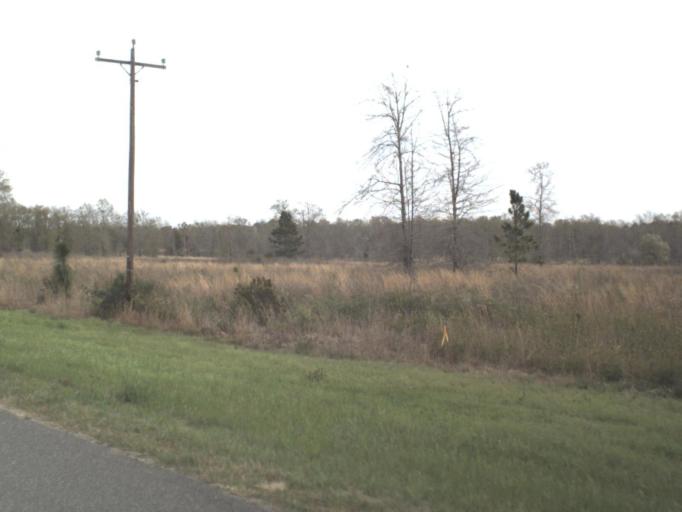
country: US
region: Florida
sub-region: Holmes County
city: Bonifay
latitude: 30.7528
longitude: -85.6849
